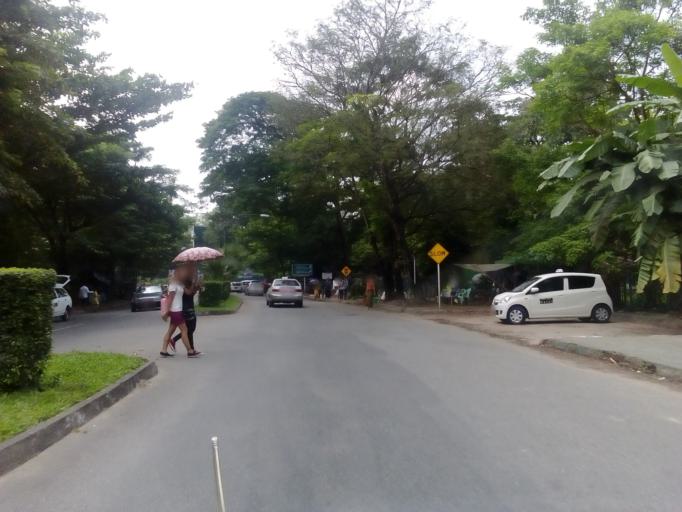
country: MM
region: Yangon
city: Yangon
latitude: 16.7888
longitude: 96.1588
